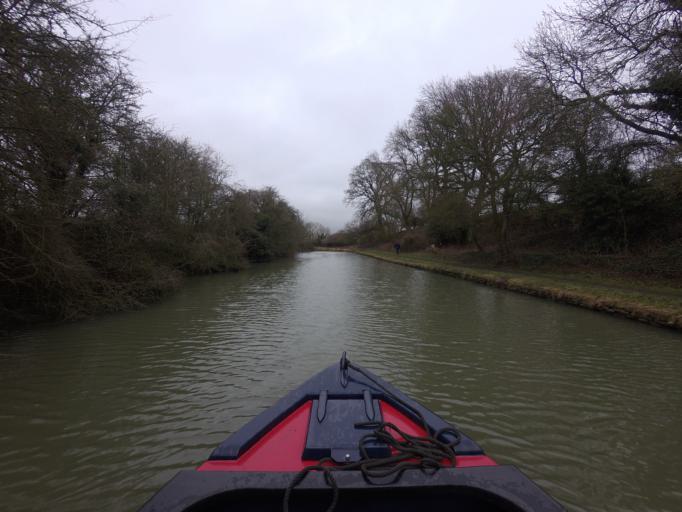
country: GB
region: England
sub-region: Northamptonshire
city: Long Buckby
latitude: 52.2839
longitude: -1.1223
